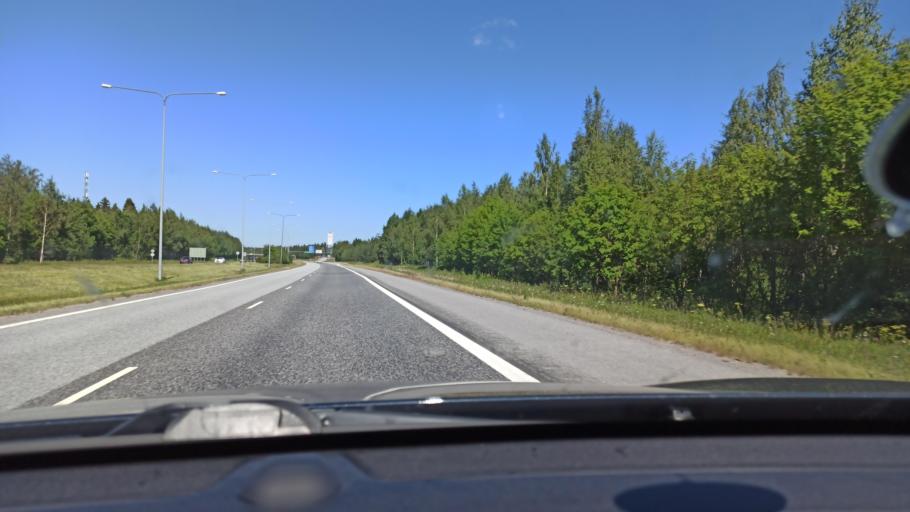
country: FI
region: Ostrobothnia
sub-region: Vaasa
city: Ristinummi
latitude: 63.0643
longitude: 21.7059
